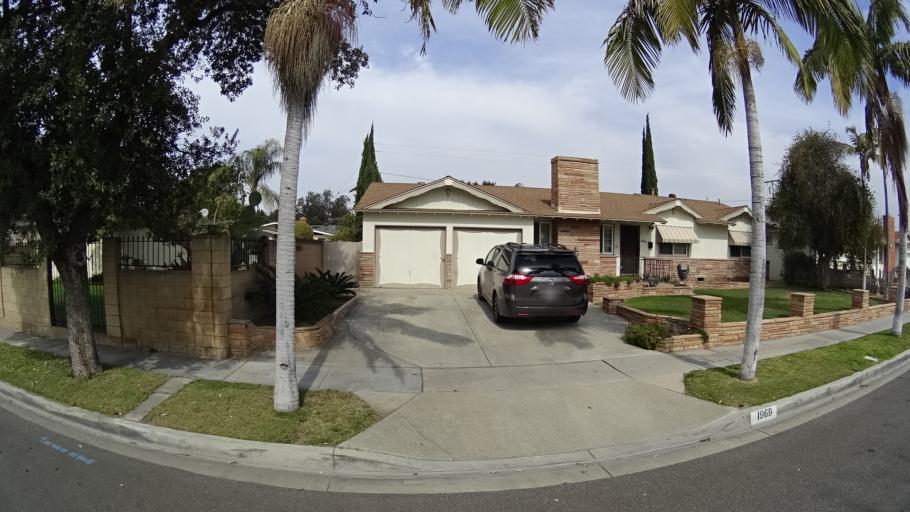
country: US
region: California
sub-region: Orange County
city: Garden Grove
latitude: 33.8114
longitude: -117.9538
